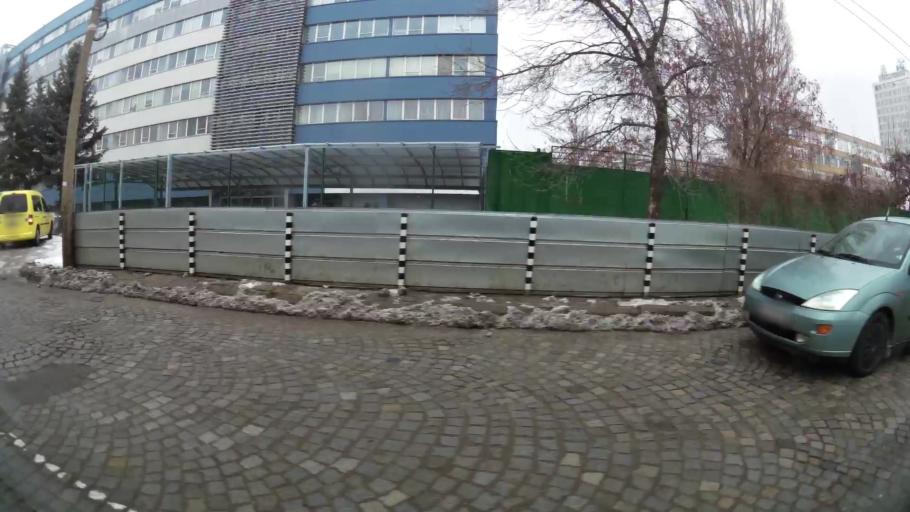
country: BG
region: Sofia-Capital
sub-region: Stolichna Obshtina
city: Sofia
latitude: 42.7170
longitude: 23.2940
